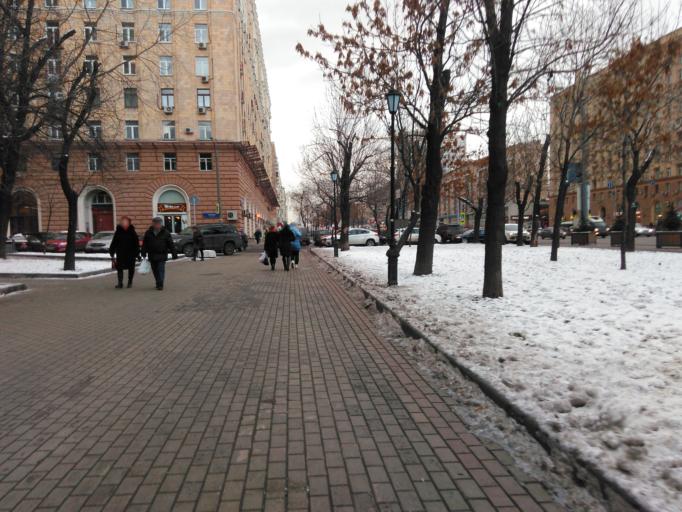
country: RU
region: Moscow
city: Mar'ina Roshcha
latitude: 55.8118
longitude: 37.6383
